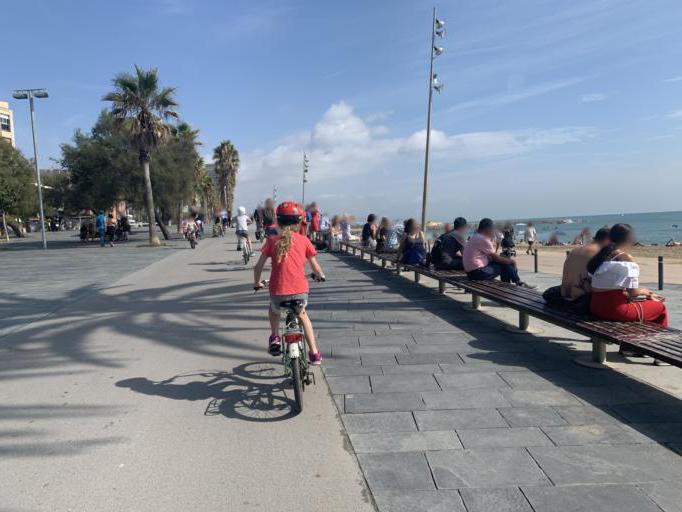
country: ES
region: Catalonia
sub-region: Provincia de Barcelona
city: Ciutat Vella
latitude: 41.3782
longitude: 2.1918
